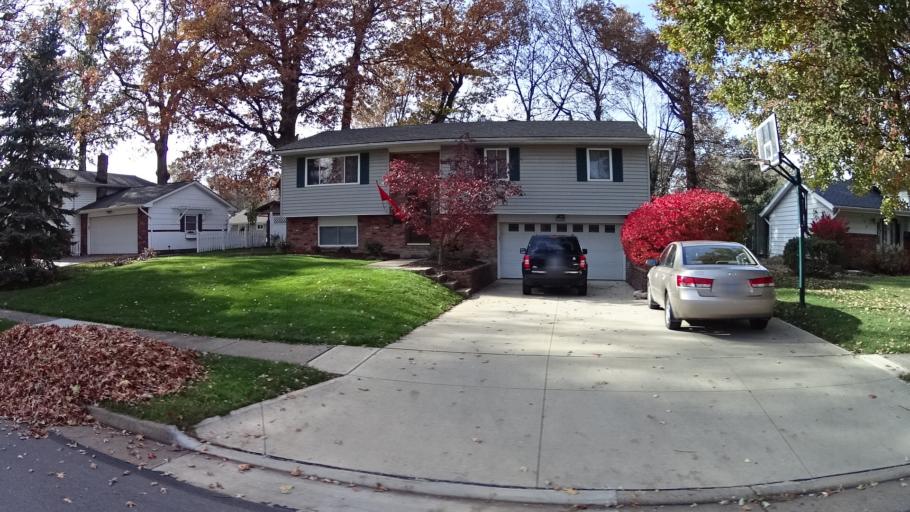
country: US
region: Ohio
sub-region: Lorain County
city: Avon Lake
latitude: 41.5054
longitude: -82.0279
